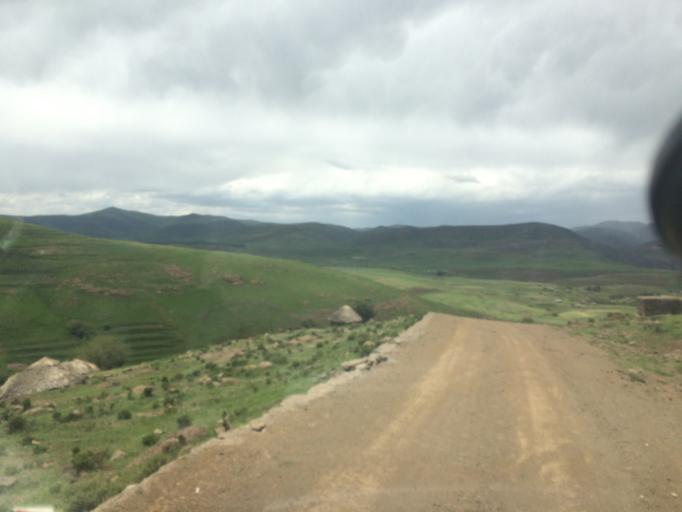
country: LS
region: Maseru
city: Nako
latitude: -29.8539
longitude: 28.0308
